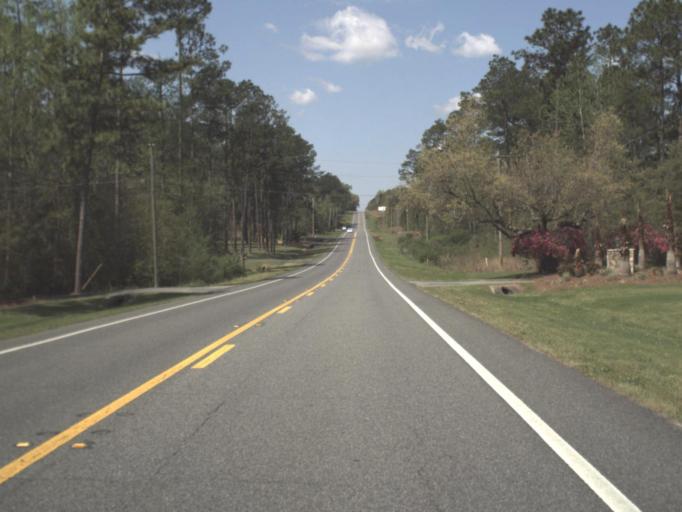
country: US
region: Alabama
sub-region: Escambia County
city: East Brewton
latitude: 30.9519
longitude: -87.1001
